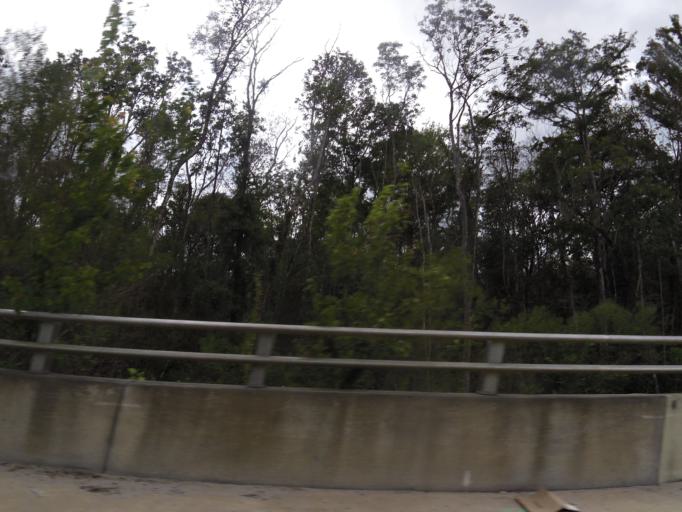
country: US
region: Florida
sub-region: Clay County
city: Asbury Lake
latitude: 30.0796
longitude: -81.8096
